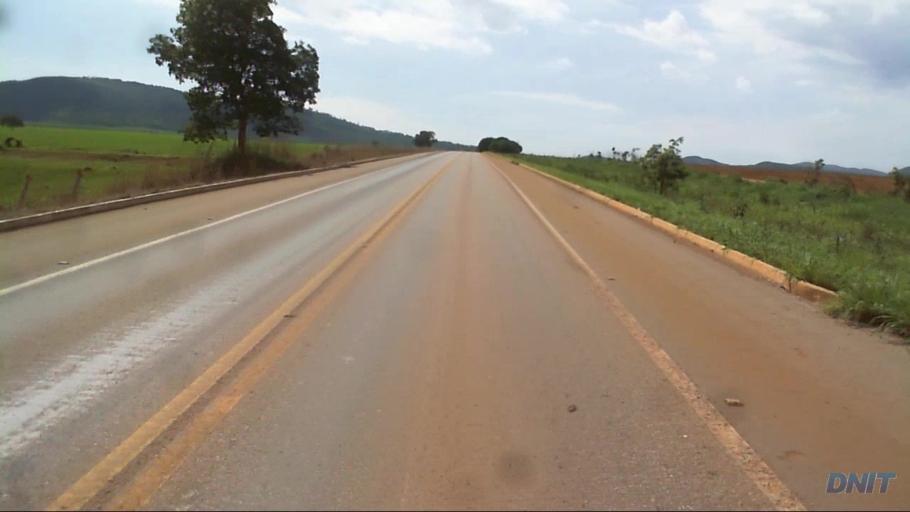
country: BR
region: Goias
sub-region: Barro Alto
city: Barro Alto
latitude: -15.0995
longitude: -48.8517
